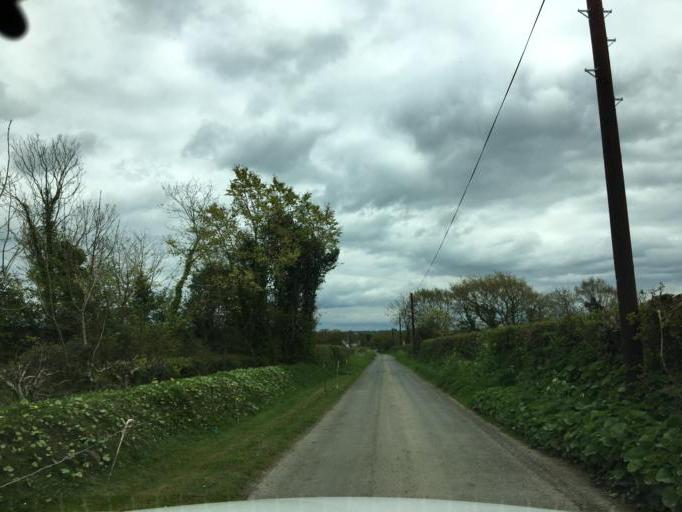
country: IE
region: Leinster
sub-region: Loch Garman
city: New Ross
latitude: 52.4328
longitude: -6.9812
